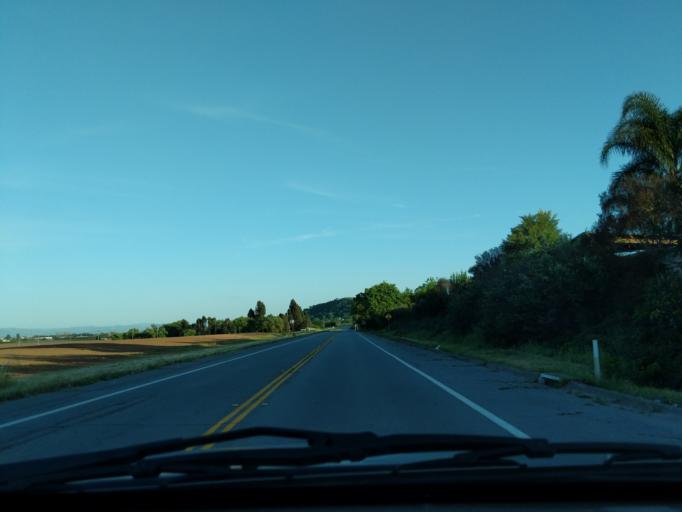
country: US
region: California
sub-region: Santa Clara County
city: Gilroy
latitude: 36.9791
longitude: -121.5701
